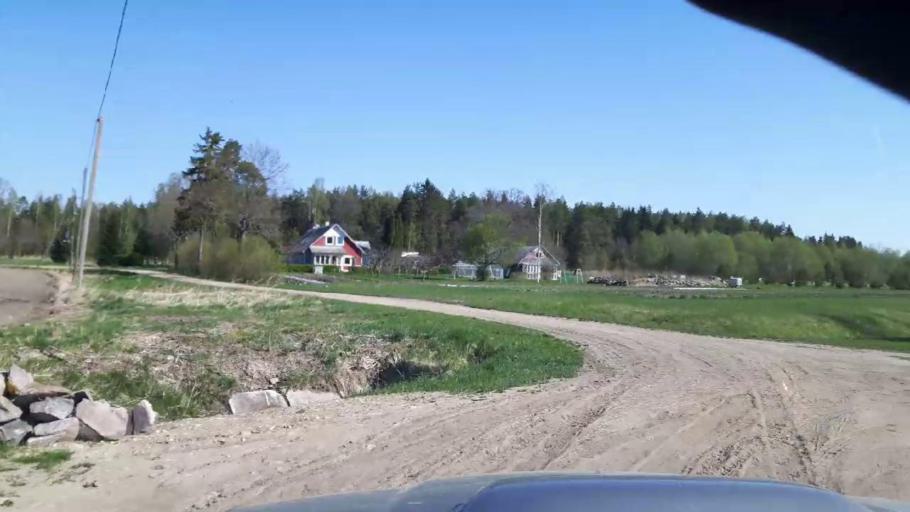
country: EE
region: Paernumaa
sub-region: Tootsi vald
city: Tootsi
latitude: 58.4519
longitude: 24.7834
